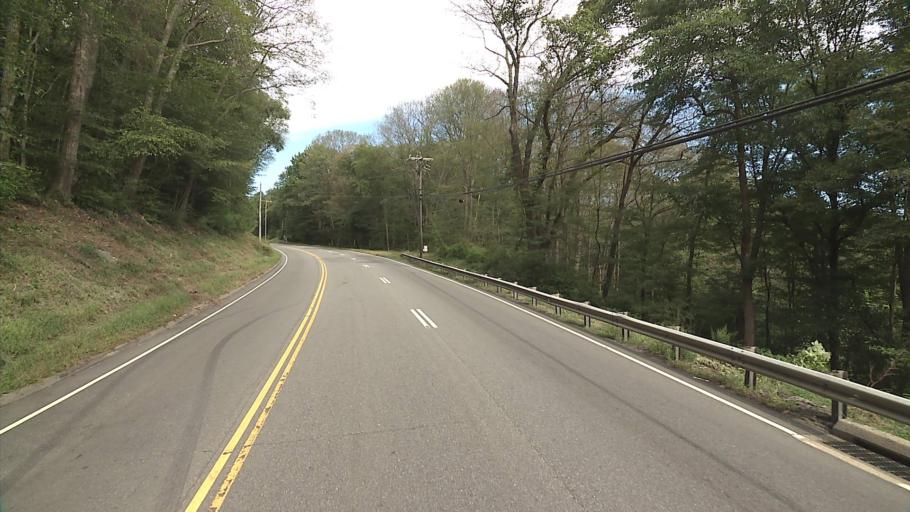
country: US
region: Connecticut
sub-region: New London County
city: Baltic
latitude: 41.6162
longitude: -72.1459
